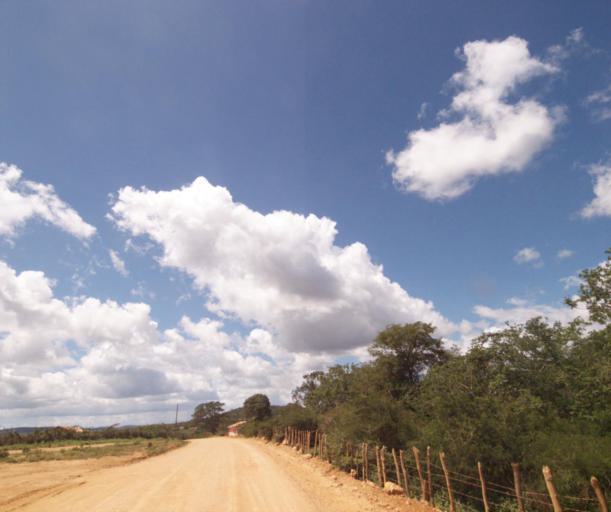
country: BR
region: Bahia
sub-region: Pocoes
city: Pocoes
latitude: -14.3396
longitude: -40.5938
